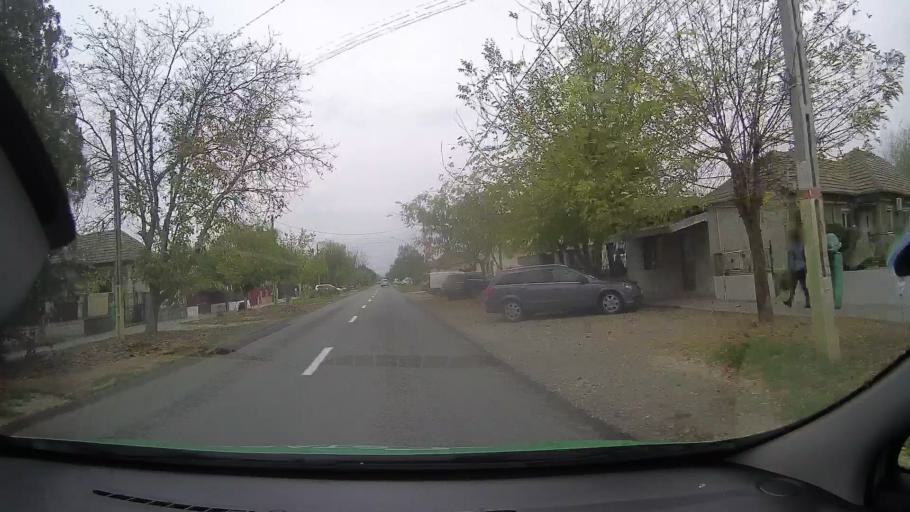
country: RO
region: Constanta
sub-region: Comuna Mihail Kogalniceanu
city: Mihail Kogalniceanu
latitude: 44.3703
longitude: 28.4633
